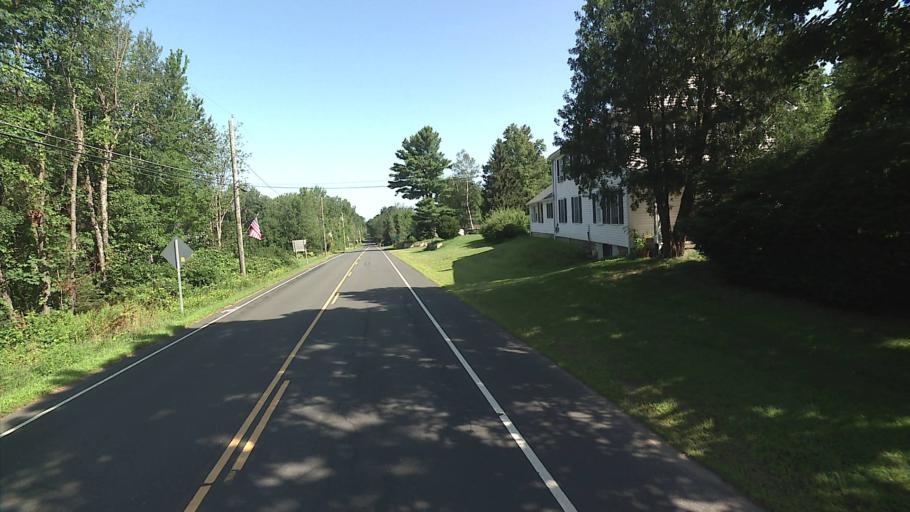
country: US
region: Connecticut
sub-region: Hartford County
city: North Granby
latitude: 41.9998
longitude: -72.9068
